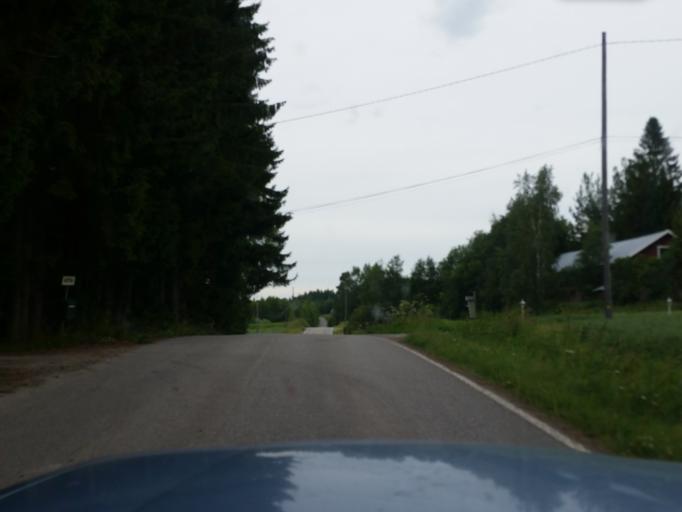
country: FI
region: Uusimaa
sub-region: Helsinki
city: Sammatti
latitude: 60.4628
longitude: 23.8483
